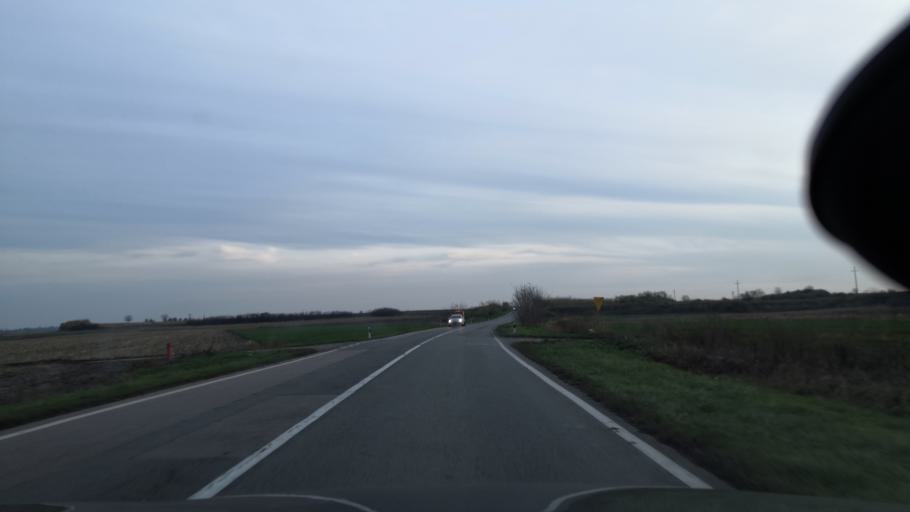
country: RS
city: Ostojicevo
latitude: 45.9068
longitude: 20.1540
